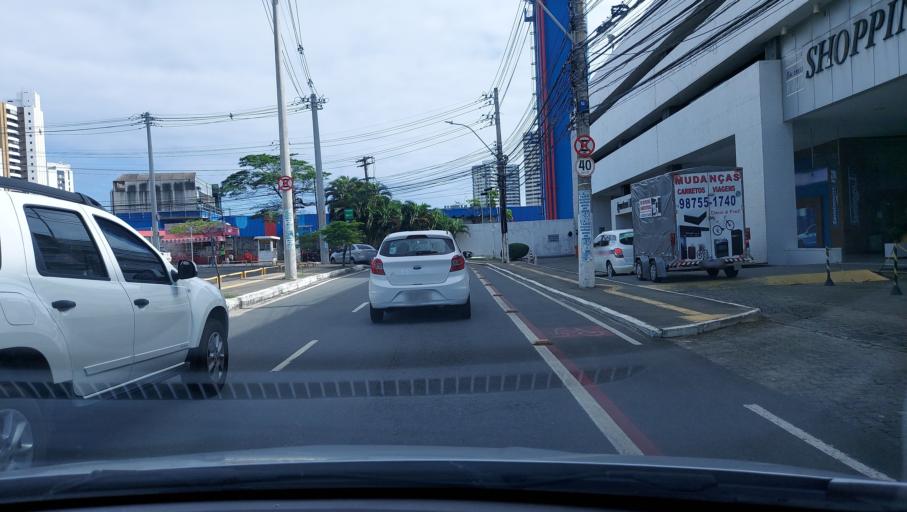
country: BR
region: Bahia
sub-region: Salvador
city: Salvador
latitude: -12.9836
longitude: -38.4646
